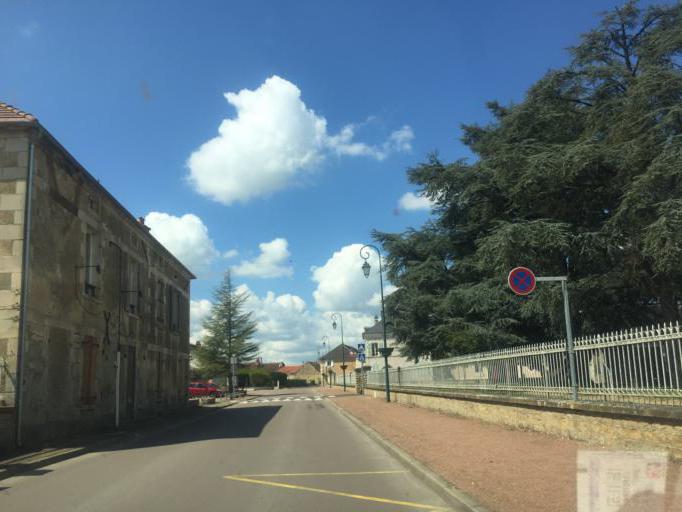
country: FR
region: Bourgogne
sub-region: Departement de l'Yonne
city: Fontenailles
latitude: 47.5038
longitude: 3.3444
